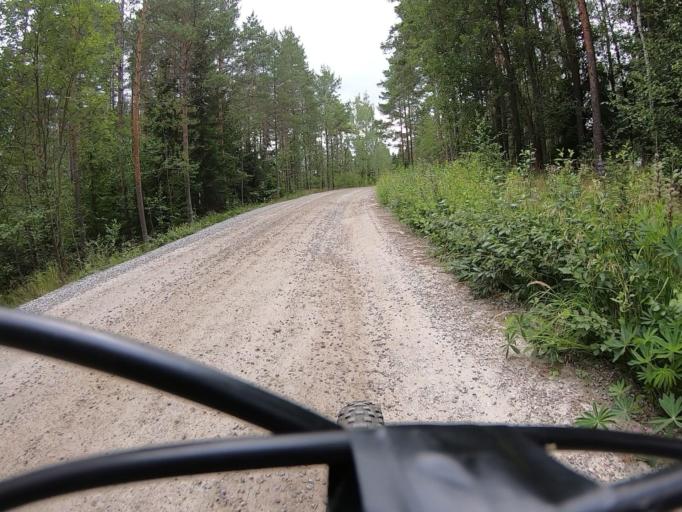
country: FI
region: Varsinais-Suomi
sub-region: Vakka-Suomi
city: Uusikaupunki
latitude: 60.8448
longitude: 21.3896
